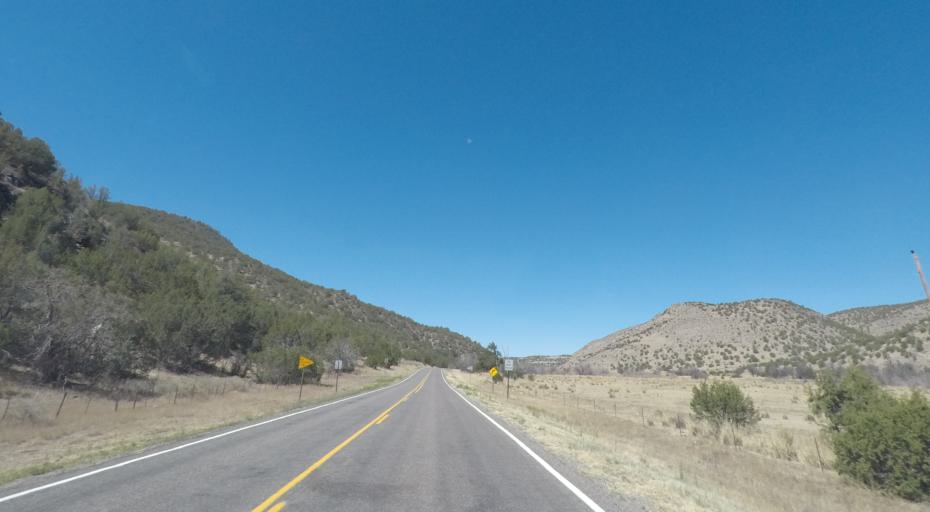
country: US
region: New Mexico
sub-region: Lincoln County
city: Capitan
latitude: 33.5268
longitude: -105.4433
